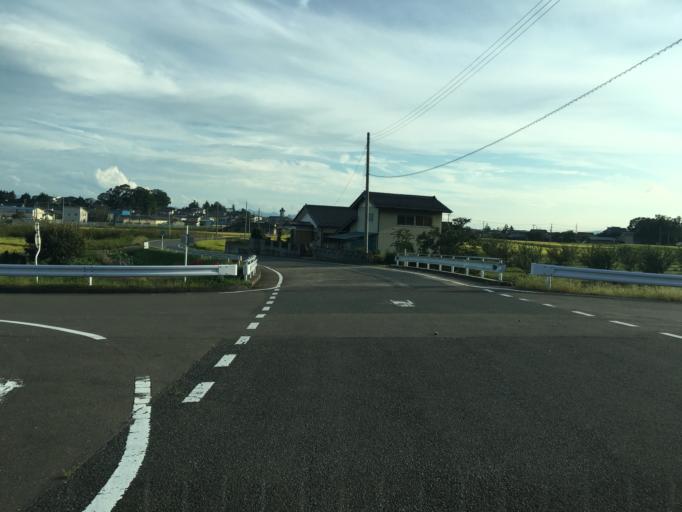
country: JP
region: Fukushima
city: Yanagawamachi-saiwaicho
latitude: 37.8841
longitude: 140.5422
